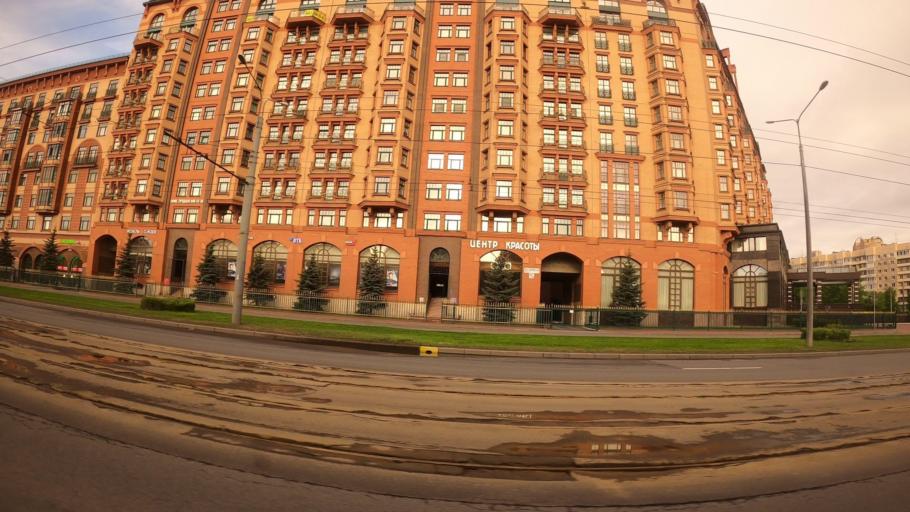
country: RU
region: St.-Petersburg
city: Vasyl'evsky Ostrov
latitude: 59.9416
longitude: 30.2319
